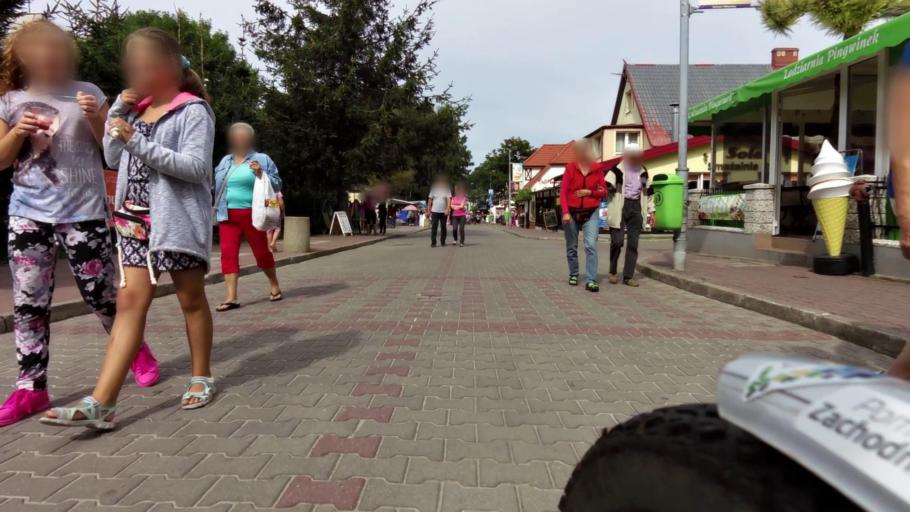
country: PL
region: West Pomeranian Voivodeship
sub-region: Powiat kolobrzeski
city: Ustronie Morskie
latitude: 54.2132
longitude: 15.7454
